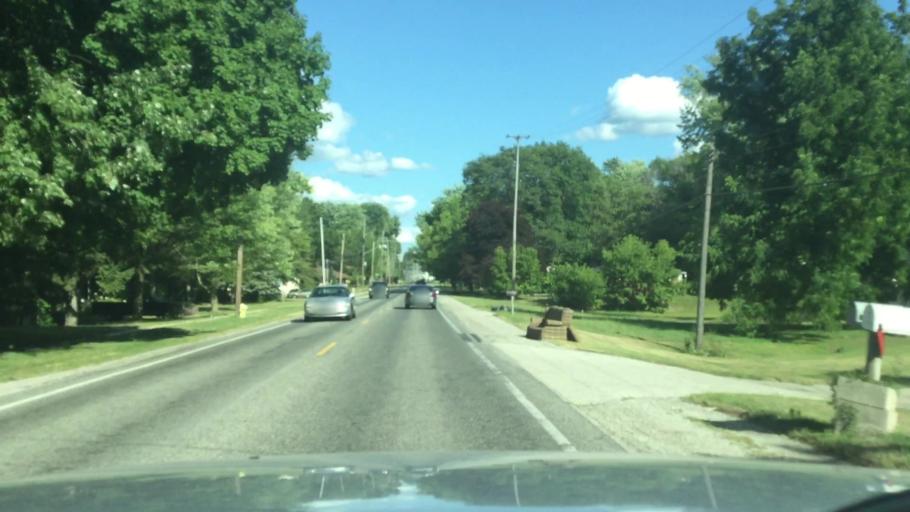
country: US
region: Michigan
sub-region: Saginaw County
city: Bridgeport
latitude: 43.3628
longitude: -83.8897
